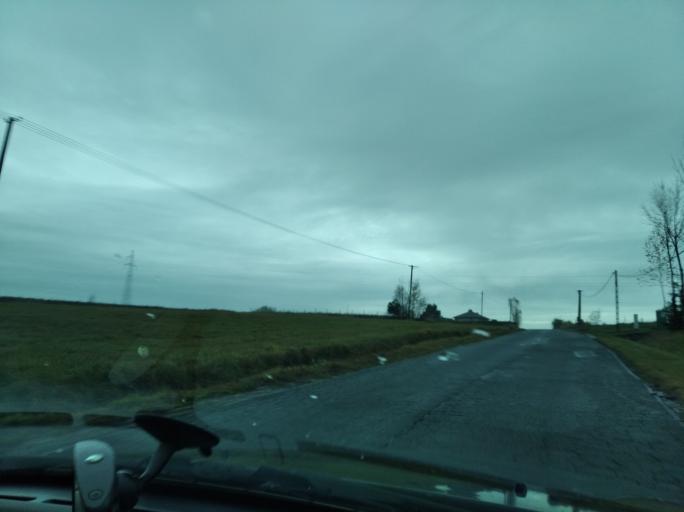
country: PL
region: Subcarpathian Voivodeship
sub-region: Powiat rzeszowski
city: Tyczyn
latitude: 49.9290
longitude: 22.0292
